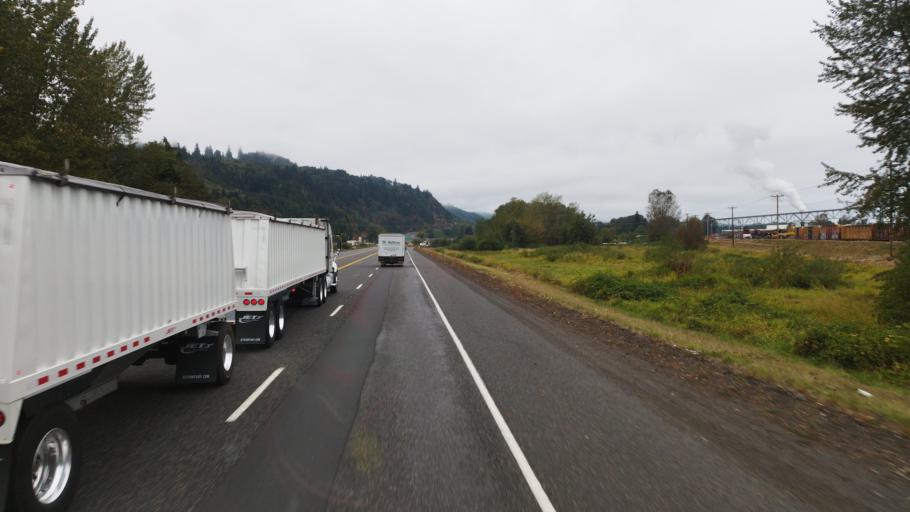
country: US
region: Oregon
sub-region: Columbia County
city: Rainier
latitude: 46.0942
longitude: -122.9543
